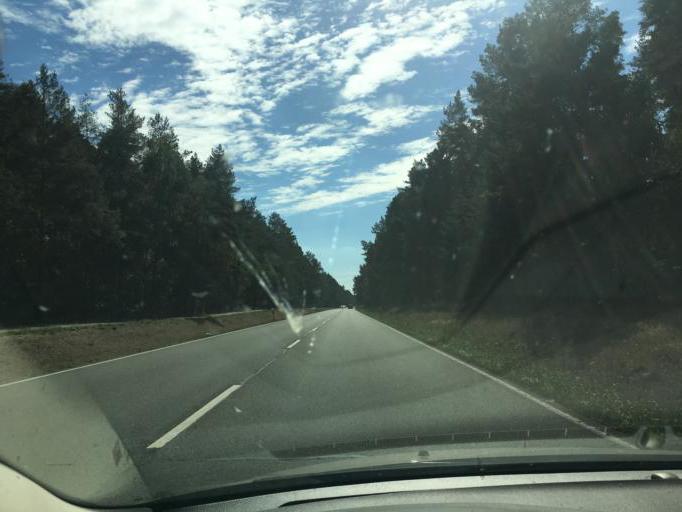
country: DE
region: Saxony-Anhalt
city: Seehausen
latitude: 52.8755
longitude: 11.7310
